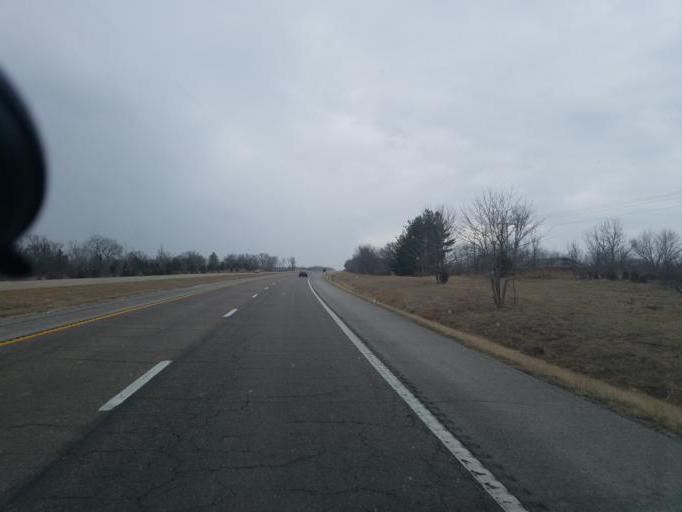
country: US
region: Missouri
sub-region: Boone County
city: Hallsville
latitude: 39.1154
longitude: -92.3292
